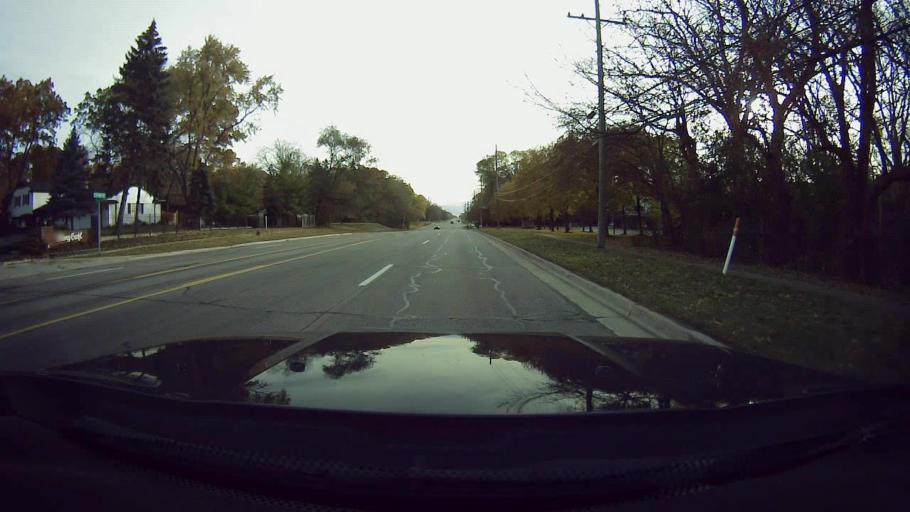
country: US
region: Michigan
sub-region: Oakland County
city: Bingham Farms
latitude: 42.4720
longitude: -83.2742
